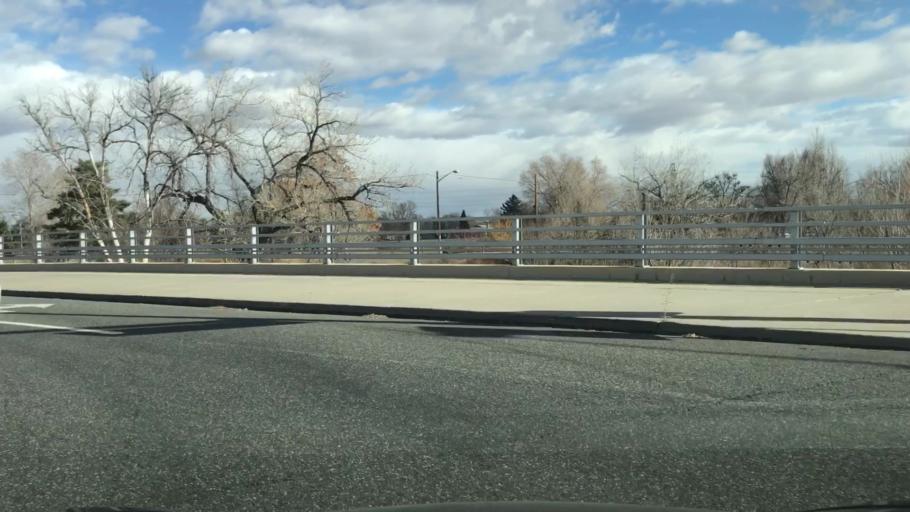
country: US
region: Colorado
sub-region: Arapahoe County
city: Glendale
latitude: 39.6960
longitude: -104.9222
